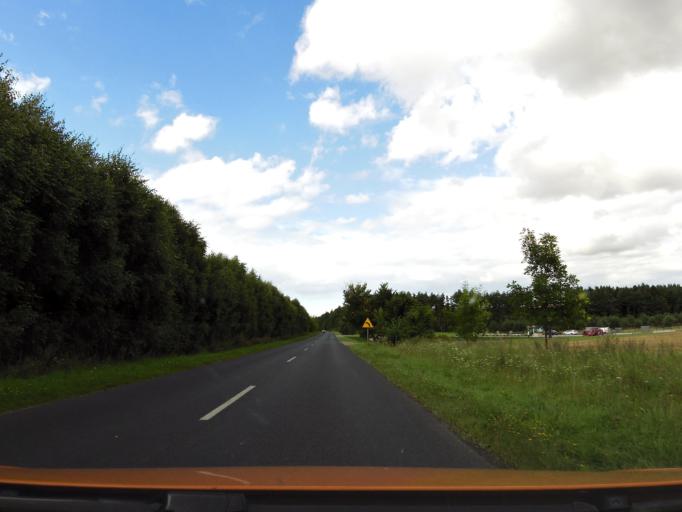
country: PL
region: West Pomeranian Voivodeship
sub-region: Powiat kolobrzeski
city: Kolobrzeg
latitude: 54.0991
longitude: 15.5793
